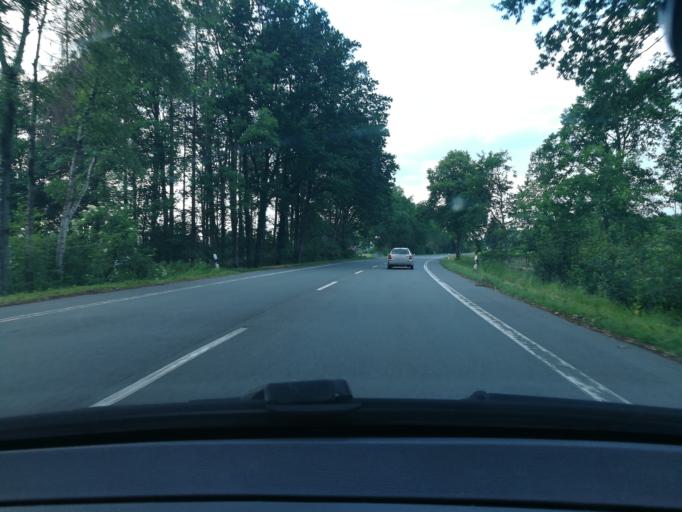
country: DE
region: North Rhine-Westphalia
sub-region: Regierungsbezirk Detmold
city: Oerlinghausen
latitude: 51.8957
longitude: 8.6703
